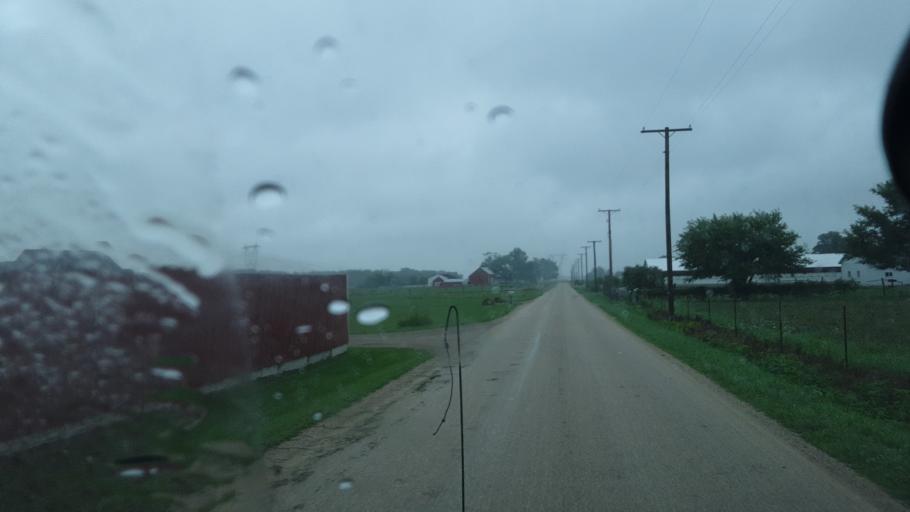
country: US
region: Indiana
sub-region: Adams County
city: Berne
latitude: 40.6872
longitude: -84.9437
